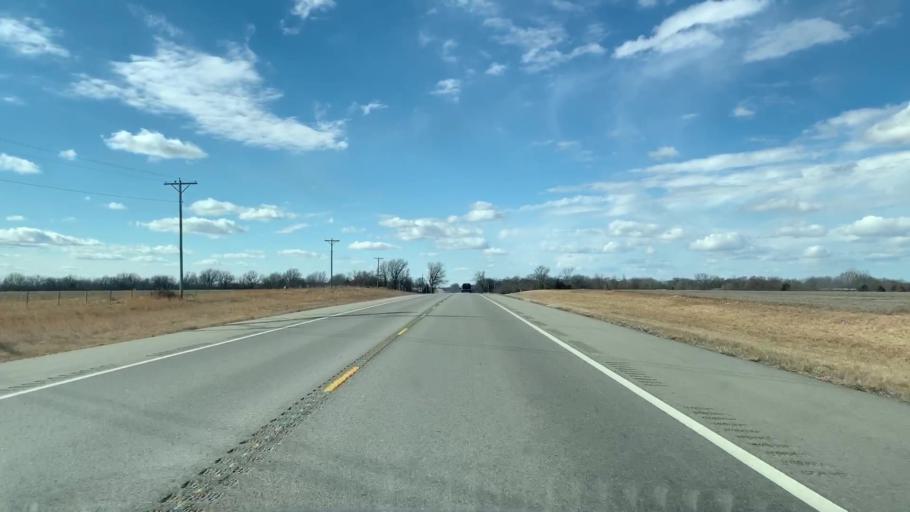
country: US
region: Kansas
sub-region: Labette County
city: Oswego
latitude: 37.3401
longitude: -95.0803
